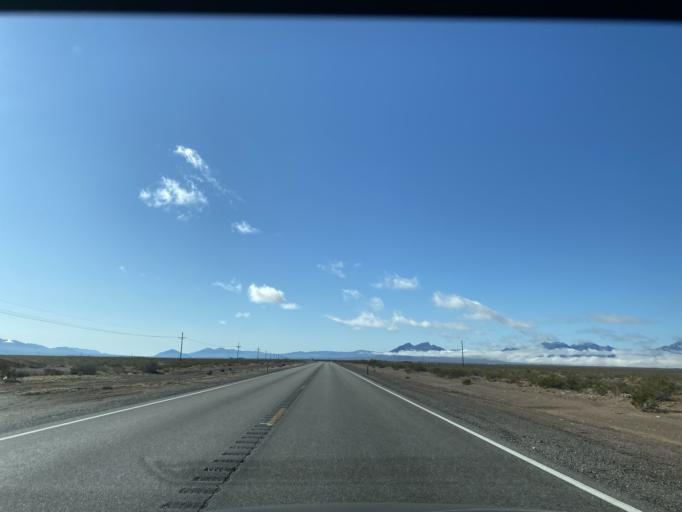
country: US
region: Nevada
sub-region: Nye County
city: Beatty
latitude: 36.5568
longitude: -116.4158
